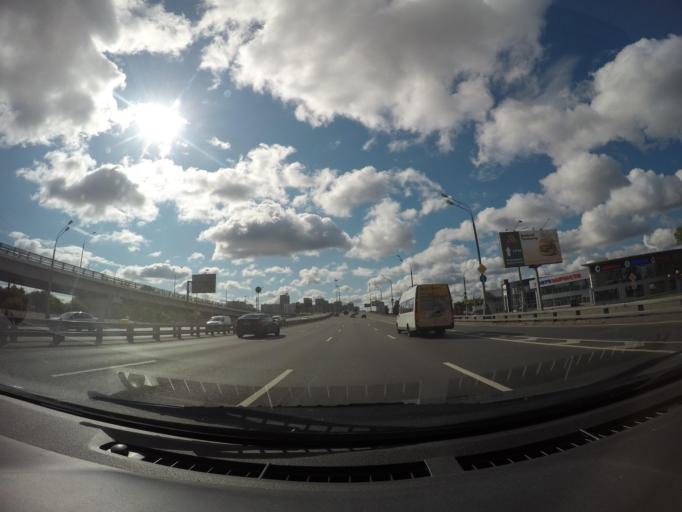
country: RU
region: Moscow
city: Khimki
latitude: 55.8763
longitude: 37.4513
